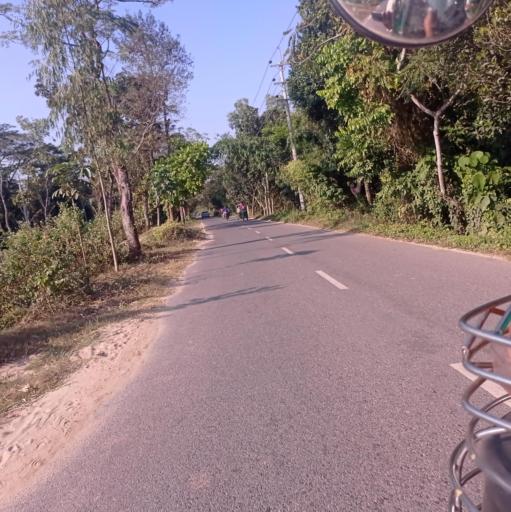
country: BD
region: Dhaka
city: Bajitpur
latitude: 24.1528
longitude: 90.8119
